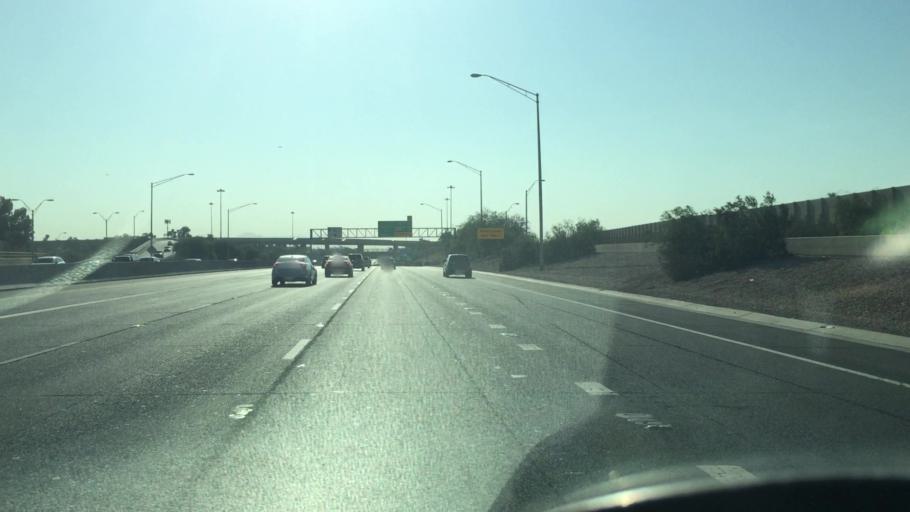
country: US
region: Arizona
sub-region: Maricopa County
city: Tempe
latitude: 33.3850
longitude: -111.8979
